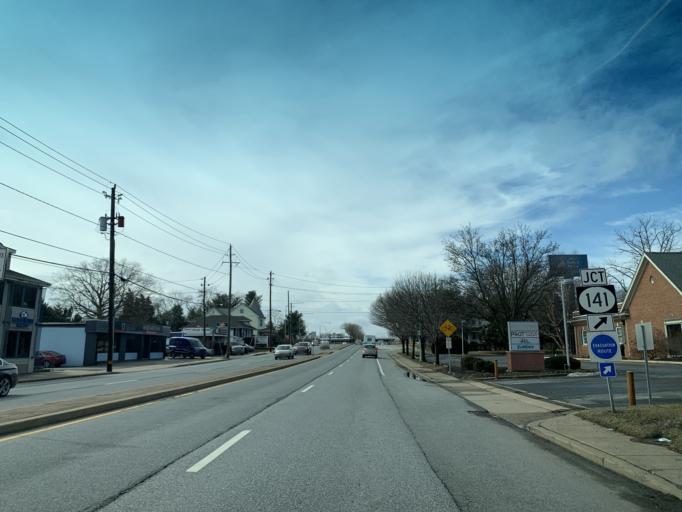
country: US
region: Delaware
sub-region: New Castle County
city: Elsmere
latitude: 39.7378
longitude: -75.6151
